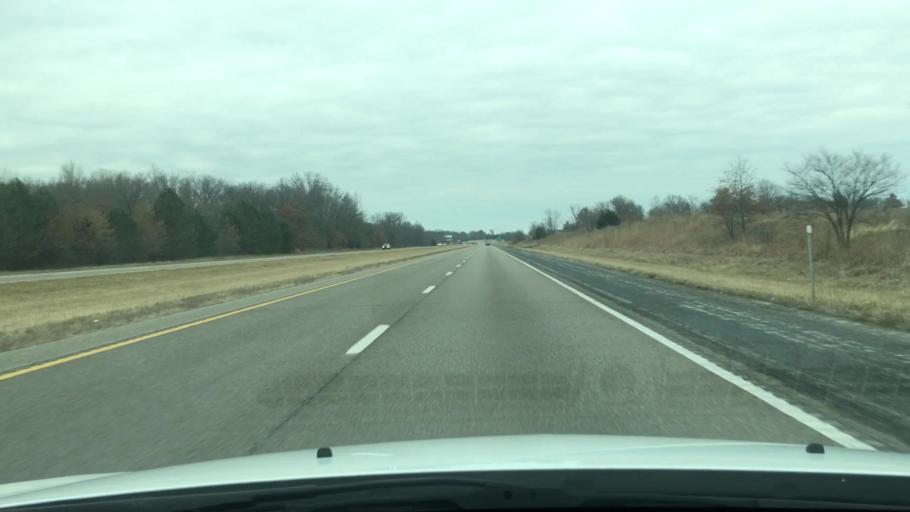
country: US
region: Missouri
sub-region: Callaway County
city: Fulton
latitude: 38.9934
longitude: -91.8935
